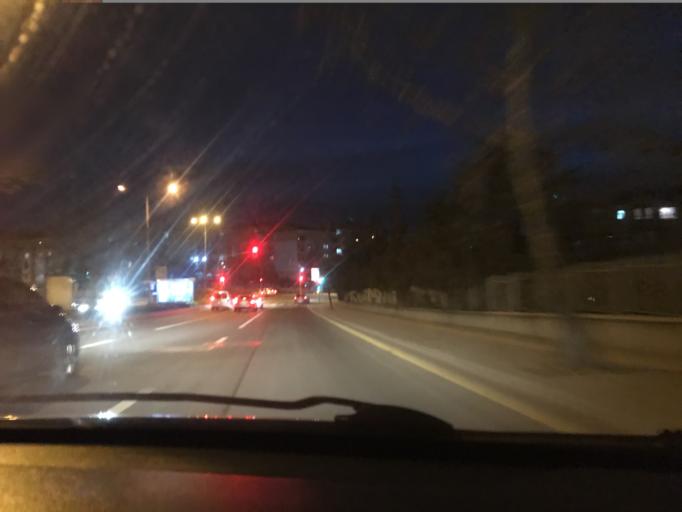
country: TR
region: Ankara
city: Batikent
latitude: 39.9590
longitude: 32.7297
